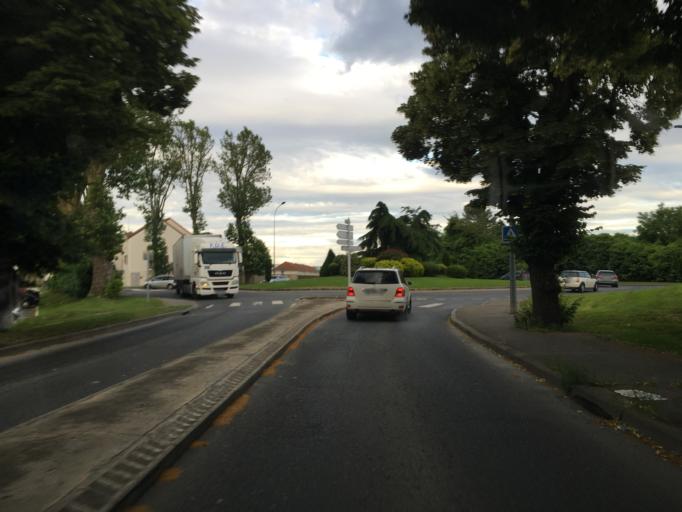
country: FR
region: Ile-de-France
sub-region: Departement du Val-de-Marne
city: Santeny
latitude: 48.7157
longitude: 2.5737
